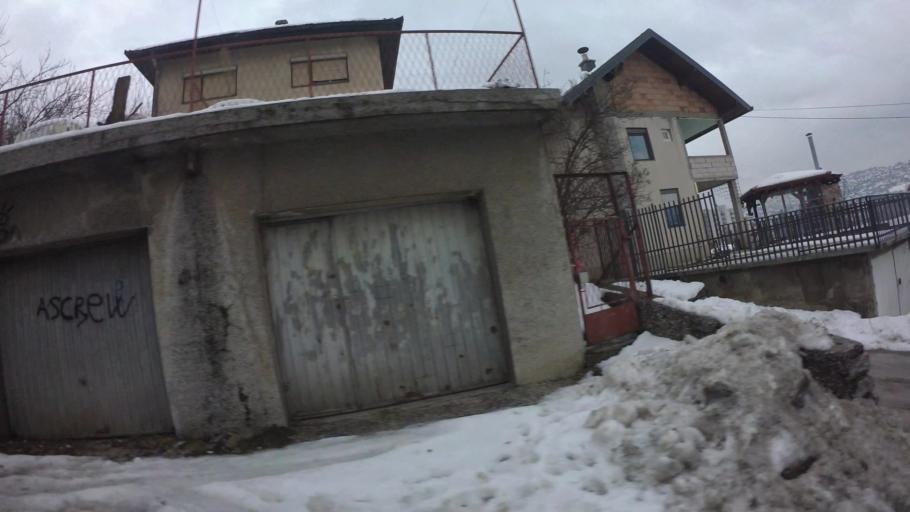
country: BA
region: Federation of Bosnia and Herzegovina
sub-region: Kanton Sarajevo
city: Sarajevo
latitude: 43.8528
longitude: 18.3539
